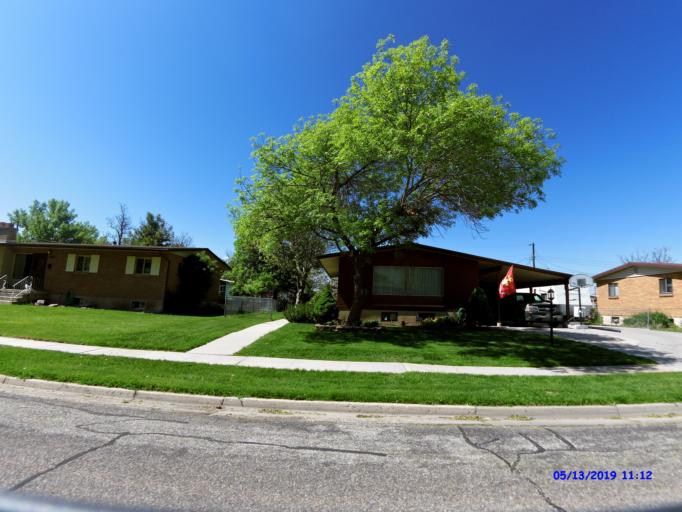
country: US
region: Utah
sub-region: Weber County
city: Harrisville
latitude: 41.2811
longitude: -111.9632
